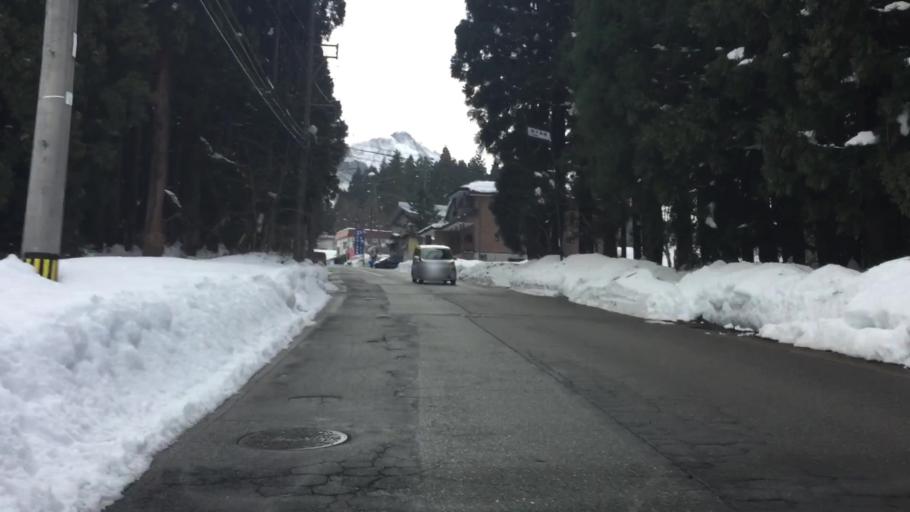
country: JP
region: Niigata
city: Shiozawa
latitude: 36.9887
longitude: 138.8217
